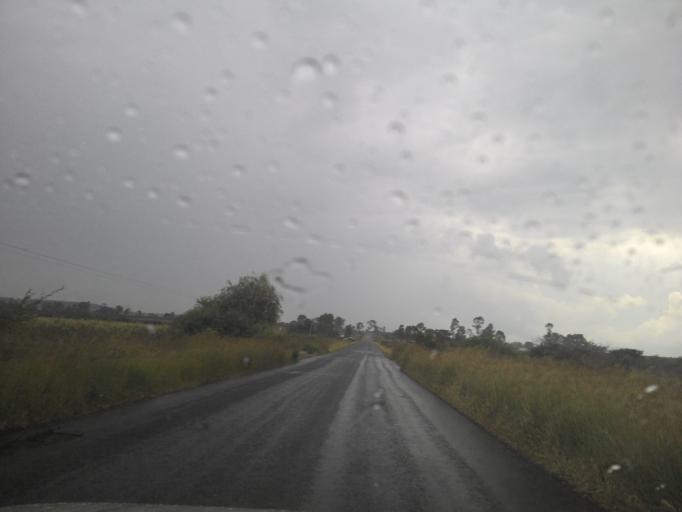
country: MX
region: Jalisco
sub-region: Arandas
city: Santiaguito (Santiaguito de Velazquez)
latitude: 20.8146
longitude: -102.2042
